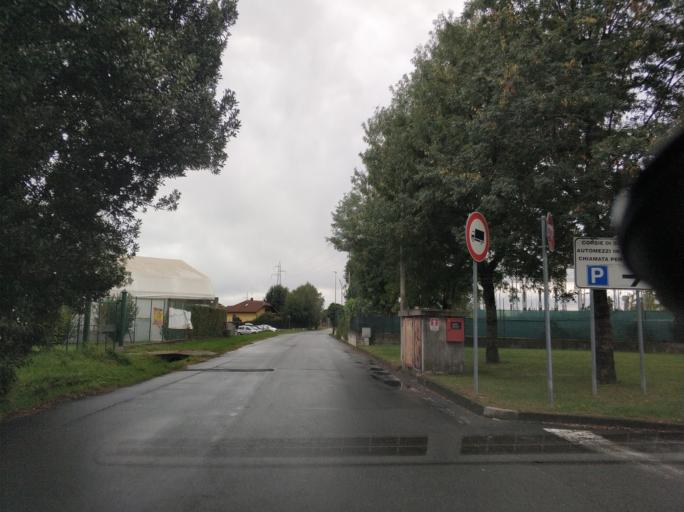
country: IT
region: Piedmont
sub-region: Provincia di Torino
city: Cirie
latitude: 45.2206
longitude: 7.5994
